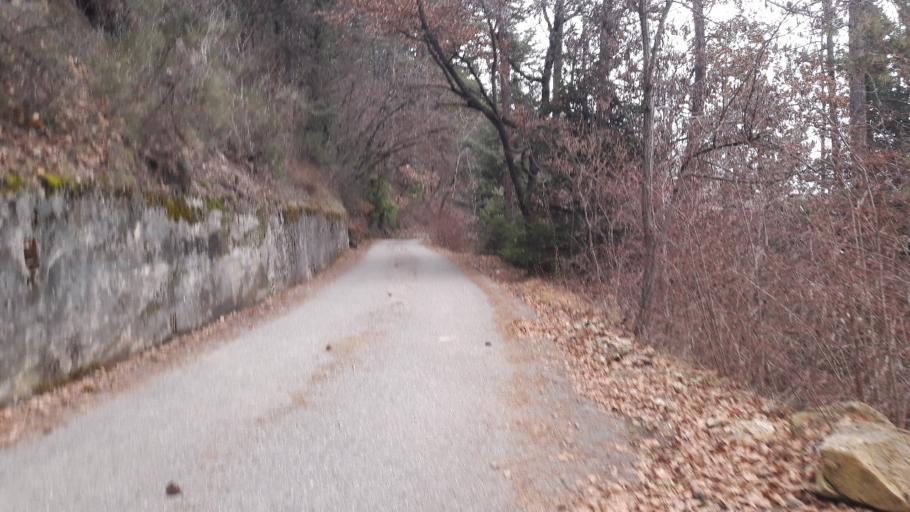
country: FR
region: Provence-Alpes-Cote d'Azur
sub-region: Departement des Alpes-de-Haute-Provence
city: Digne-les-Bains
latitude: 44.1072
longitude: 6.2257
